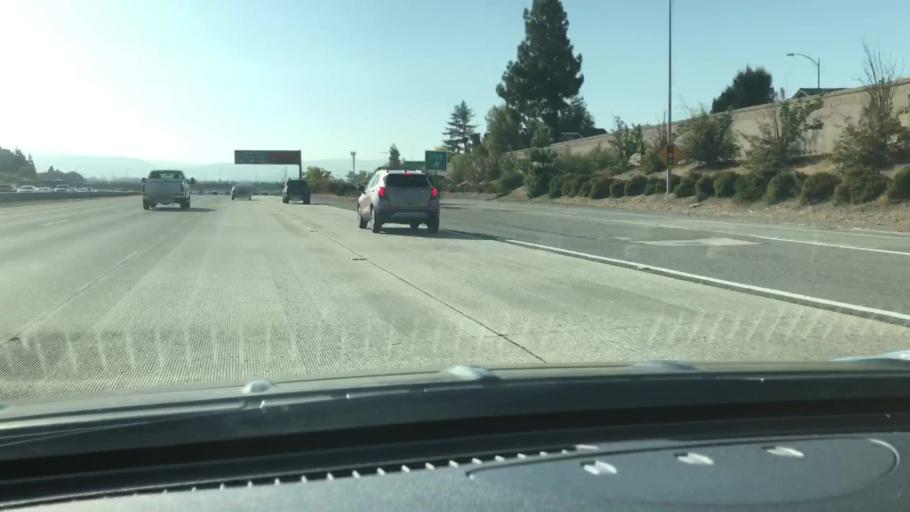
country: US
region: California
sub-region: Santa Clara County
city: Cambrian Park
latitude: 37.2537
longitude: -121.9448
